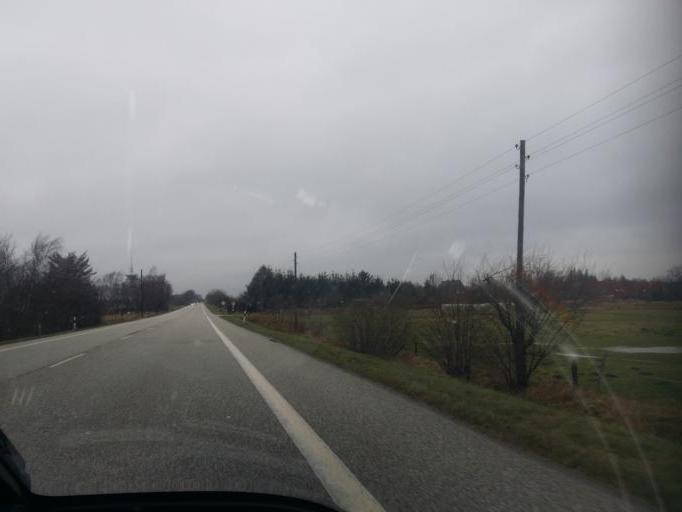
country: DE
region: Schleswig-Holstein
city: Bredstedt
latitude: 54.6339
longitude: 8.9529
